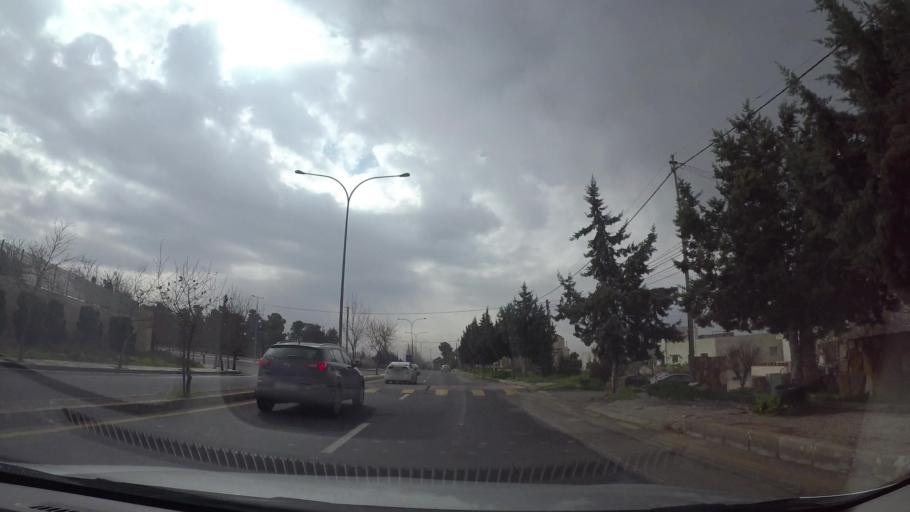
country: JO
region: Amman
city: Wadi as Sir
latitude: 31.9806
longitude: 35.8221
